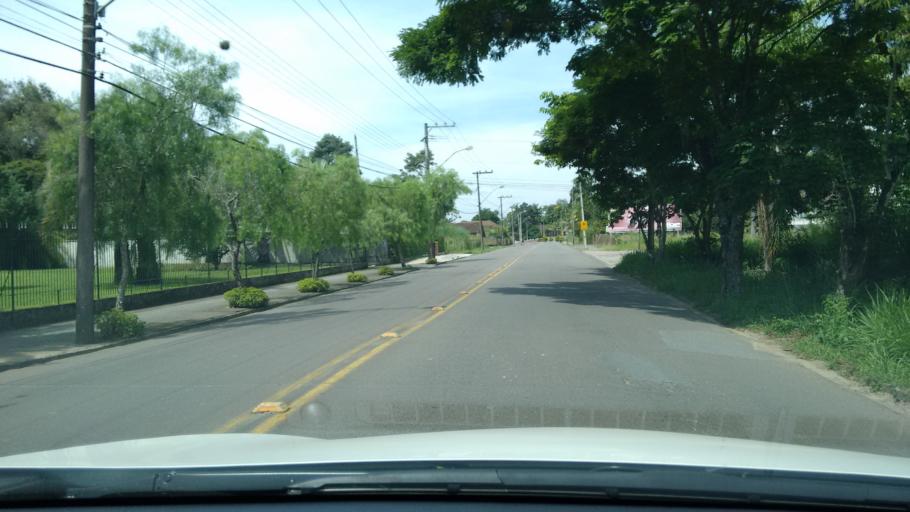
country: BR
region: Santa Catarina
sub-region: Timbo
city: Timbo
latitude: -26.8284
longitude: -49.2826
